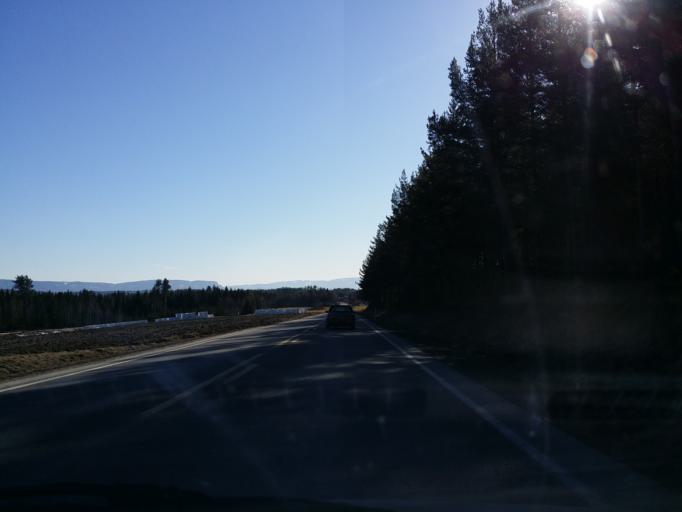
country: NO
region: Buskerud
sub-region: Ringerike
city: Honefoss
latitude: 60.2169
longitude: 10.2586
